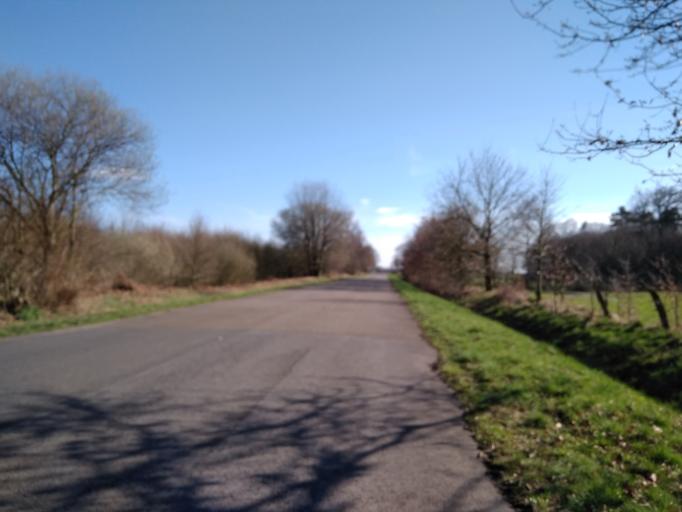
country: DE
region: North Rhine-Westphalia
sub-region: Regierungsbezirk Dusseldorf
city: Hunxe
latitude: 51.6168
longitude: 6.8430
